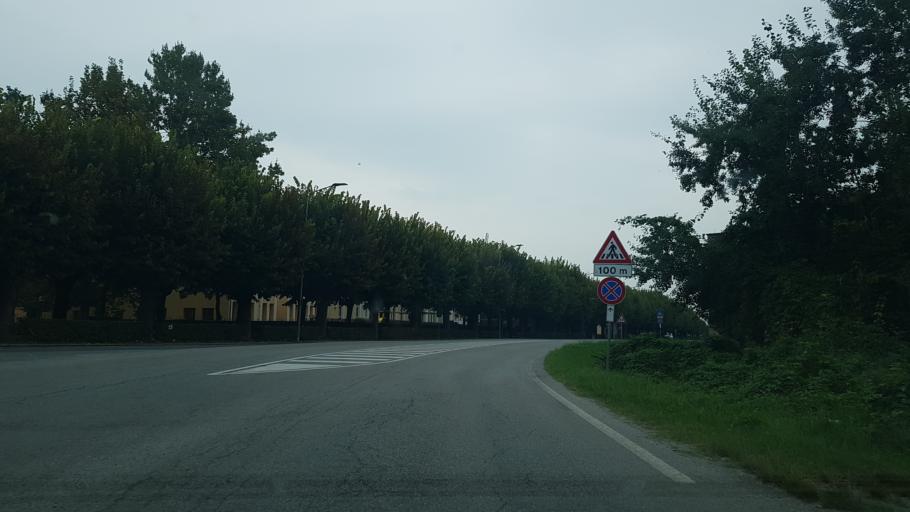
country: IT
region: Piedmont
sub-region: Provincia di Cuneo
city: Villanova Mondovi
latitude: 44.3458
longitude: 7.7669
